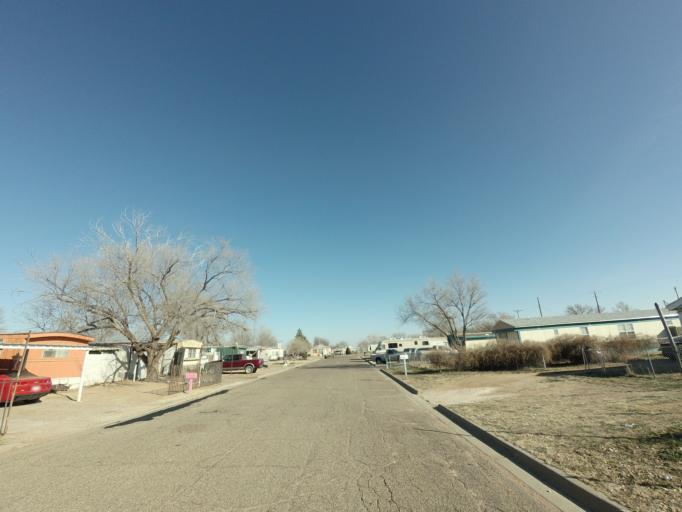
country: US
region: New Mexico
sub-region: Curry County
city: Clovis
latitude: 34.3892
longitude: -103.2020
